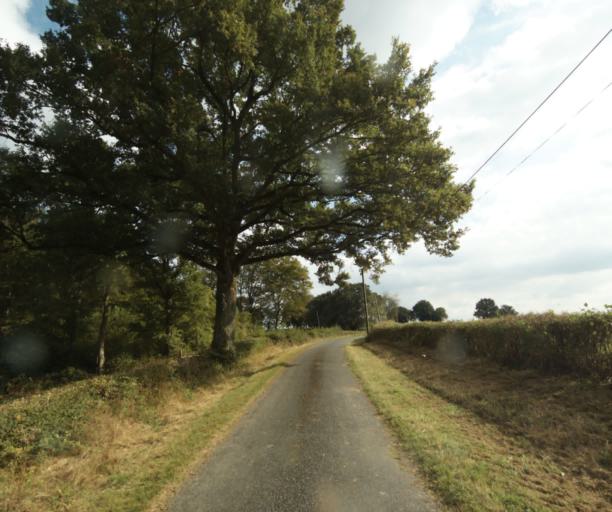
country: FR
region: Bourgogne
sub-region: Departement de Saone-et-Loire
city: Palinges
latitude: 46.5082
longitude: 4.2499
